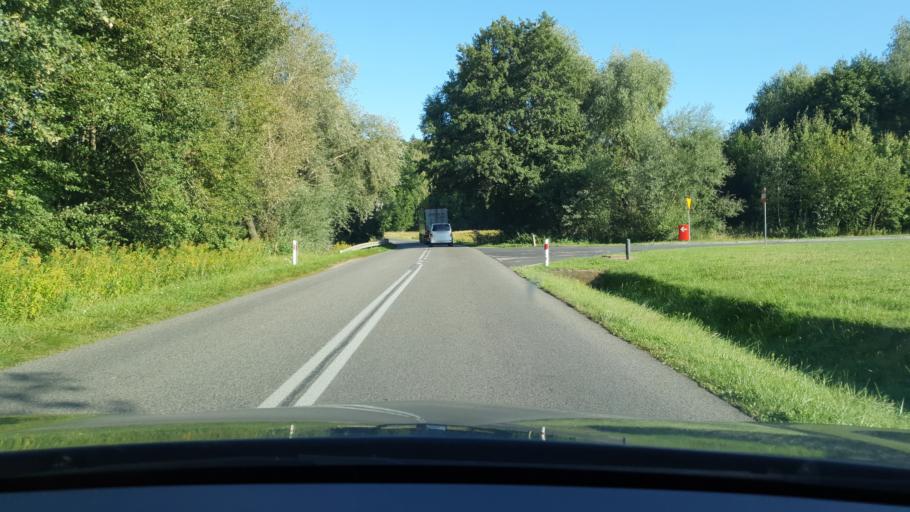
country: PL
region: West Pomeranian Voivodeship
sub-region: Powiat kamienski
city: Golczewo
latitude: 53.8215
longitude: 14.9594
